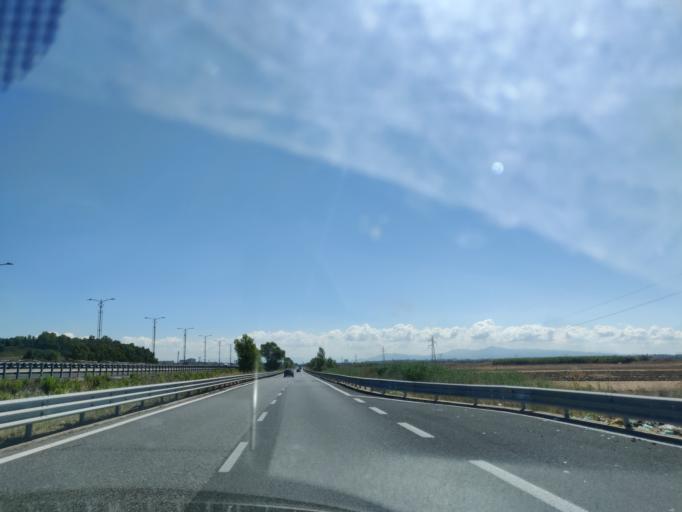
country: IT
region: Latium
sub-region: Citta metropolitana di Roma Capitale
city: Ponte Galeria-La Pisana
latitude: 41.8144
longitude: 12.3504
